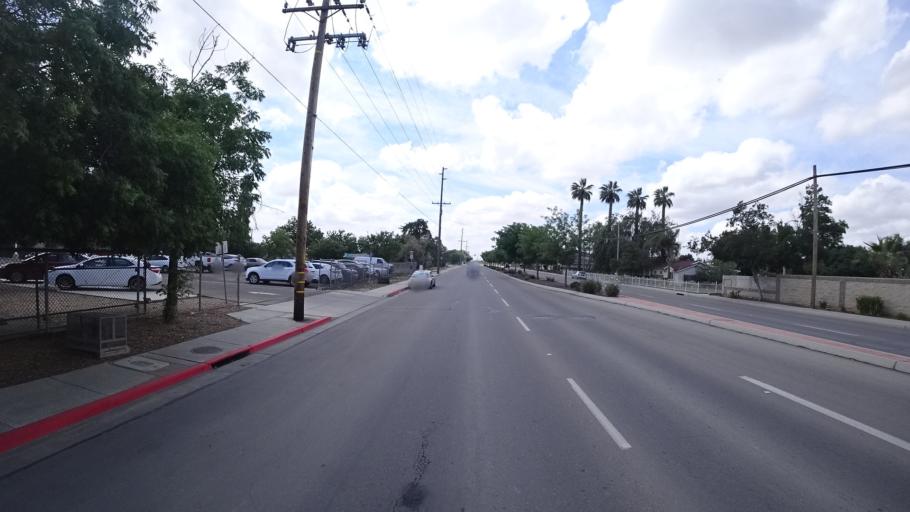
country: US
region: California
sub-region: Kings County
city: Home Garden
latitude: 36.3080
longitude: -119.6549
